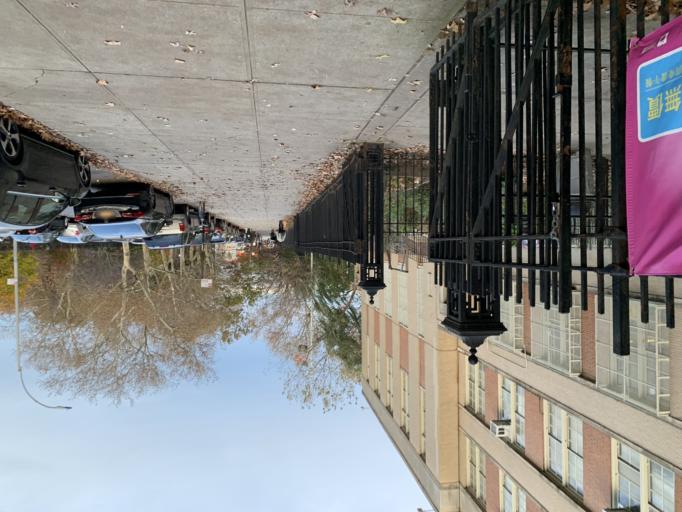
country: US
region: New York
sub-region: Queens County
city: Long Island City
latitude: 40.7222
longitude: -73.9533
